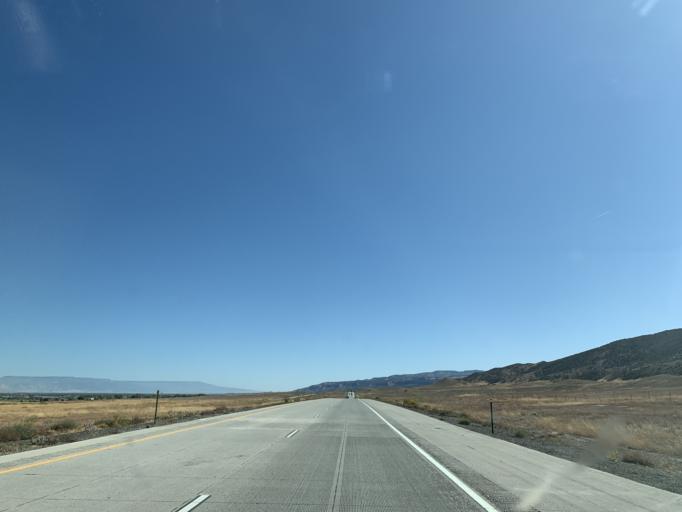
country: US
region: Colorado
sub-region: Mesa County
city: Loma
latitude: 39.2031
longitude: -108.8553
